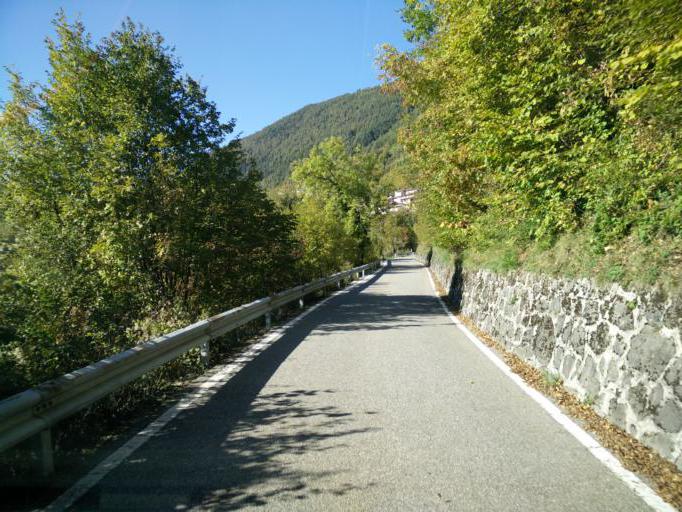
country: IT
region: Lombardy
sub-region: Provincia di Brescia
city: Capovalle
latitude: 45.7523
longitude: 10.5526
